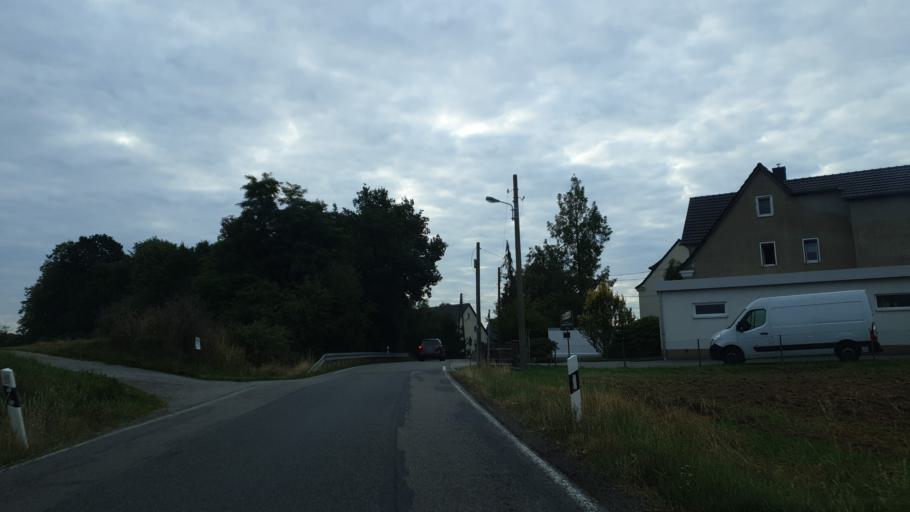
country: DE
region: Saxony
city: Callenberg
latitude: 50.8432
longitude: 12.6816
